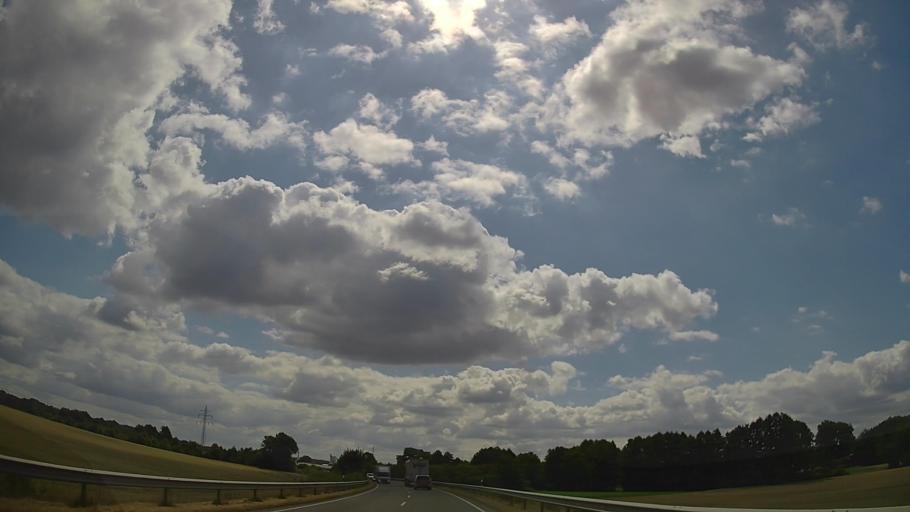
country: DE
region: Lower Saxony
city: Vechta
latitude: 52.7058
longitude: 8.2666
